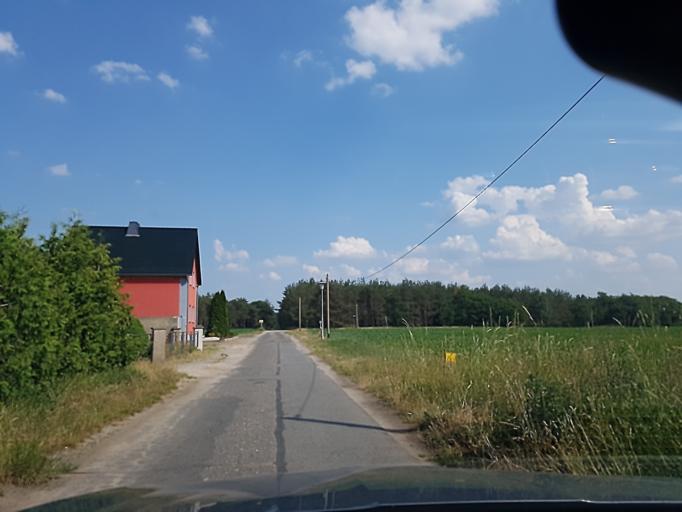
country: DE
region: Brandenburg
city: Ruckersdorf
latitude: 51.5615
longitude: 13.5579
